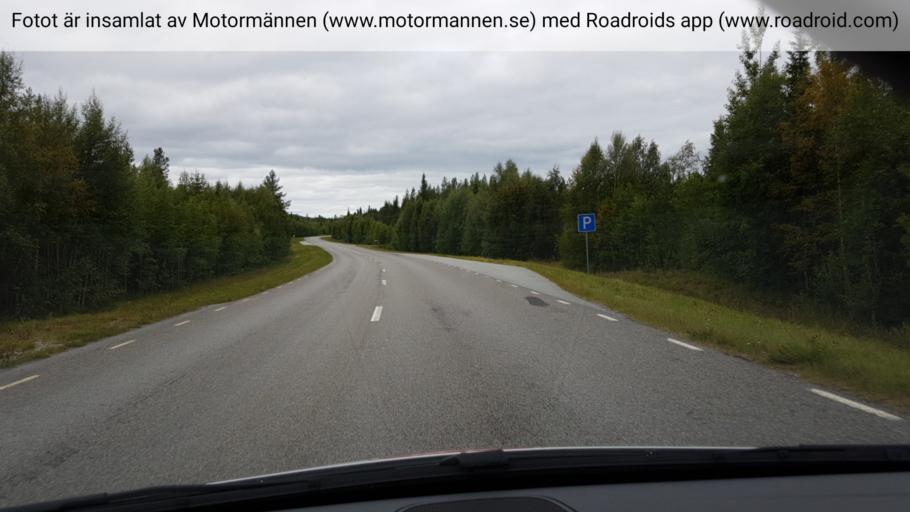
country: SE
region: Jaemtland
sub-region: Stroemsunds Kommun
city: Stroemsund
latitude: 64.3059
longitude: 15.2831
